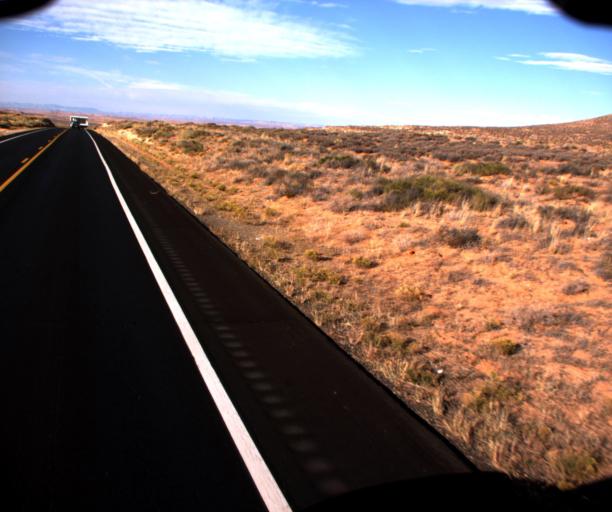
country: US
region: Arizona
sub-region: Apache County
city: Many Farms
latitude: 36.9482
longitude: -109.5246
